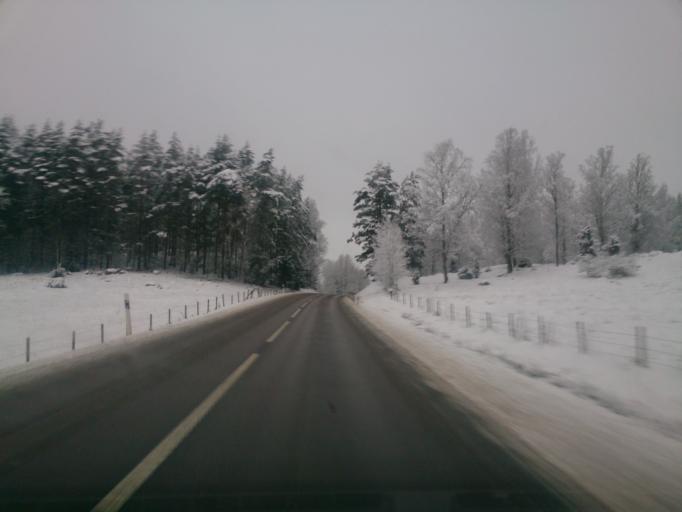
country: SE
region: OEstergoetland
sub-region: Atvidabergs Kommun
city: Atvidaberg
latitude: 58.2992
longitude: 15.8895
